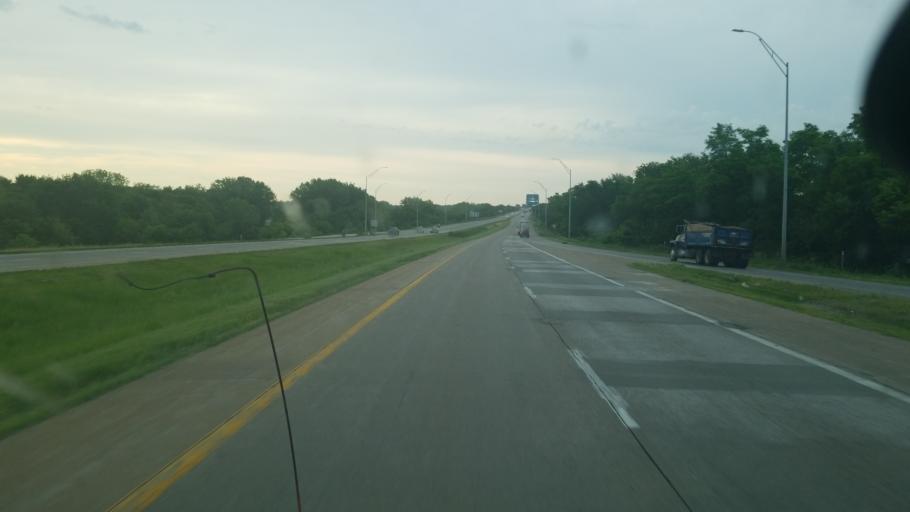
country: US
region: Illinois
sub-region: Rock Island County
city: Rock Island
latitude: 41.4899
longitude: -90.6469
